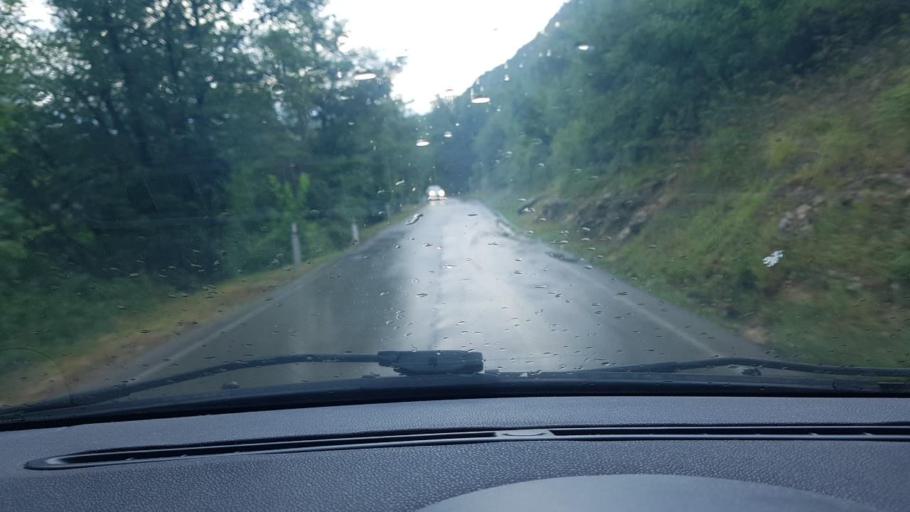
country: IT
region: Veneto
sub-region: Provincia di Verona
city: Torri del Benaco
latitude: 45.5937
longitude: 10.7008
